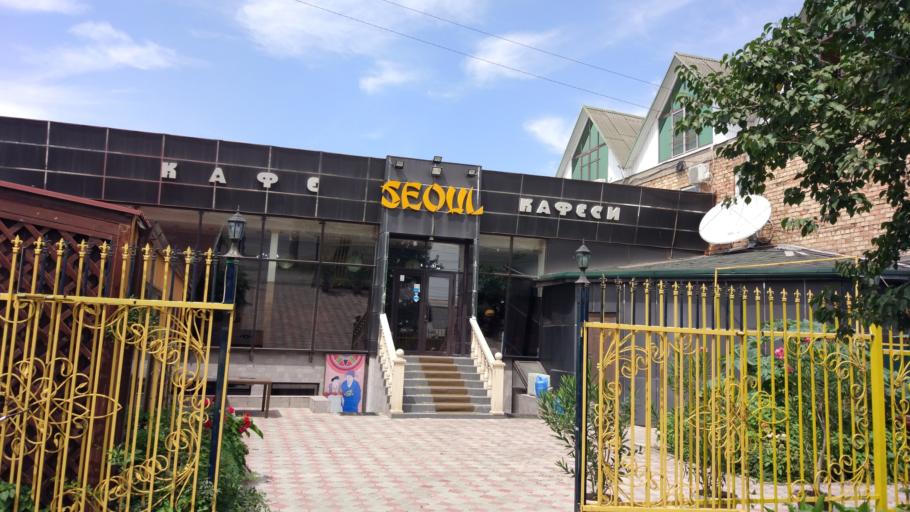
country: KG
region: Chuy
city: Bishkek
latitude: 42.8439
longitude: 74.6226
